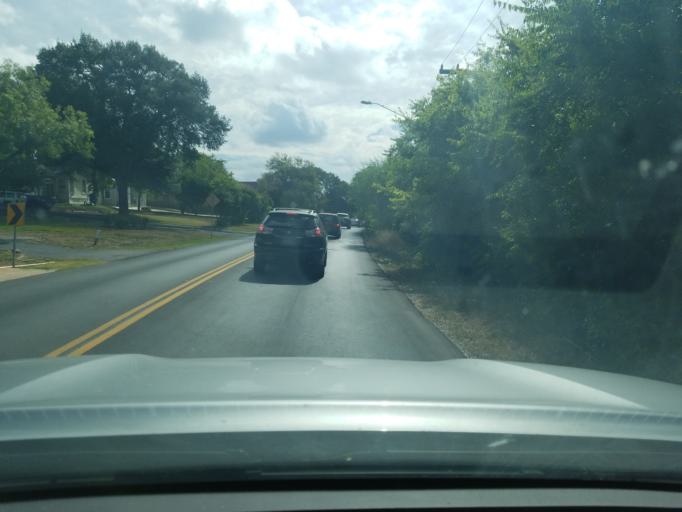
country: US
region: Texas
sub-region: Bexar County
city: Terrell Hills
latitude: 29.4701
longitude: -98.4425
